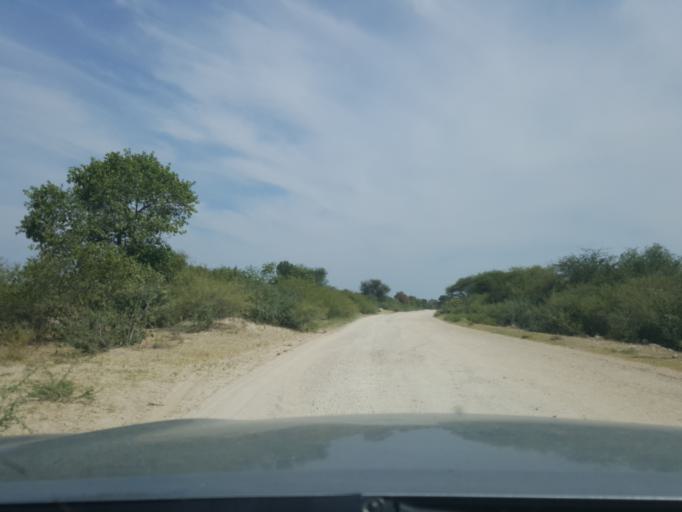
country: BW
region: North West
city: Shakawe
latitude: -18.3179
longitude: 21.9068
